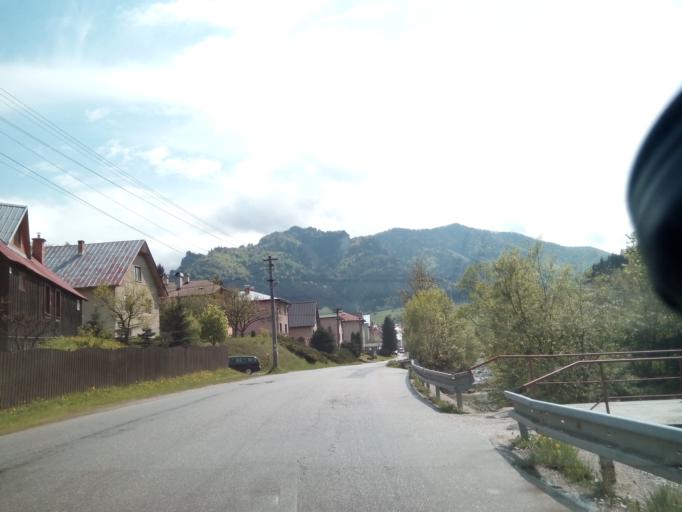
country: SK
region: Zilinsky
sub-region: Okres Zilina
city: Terchova
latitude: 49.2641
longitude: 19.0337
